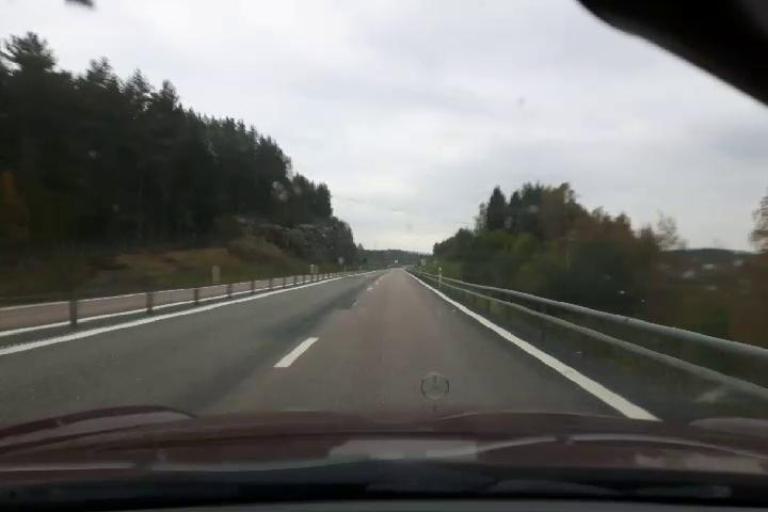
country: SE
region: Vaesternorrland
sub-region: Kramfors Kommun
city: Nordingra
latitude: 62.9253
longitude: 18.0987
